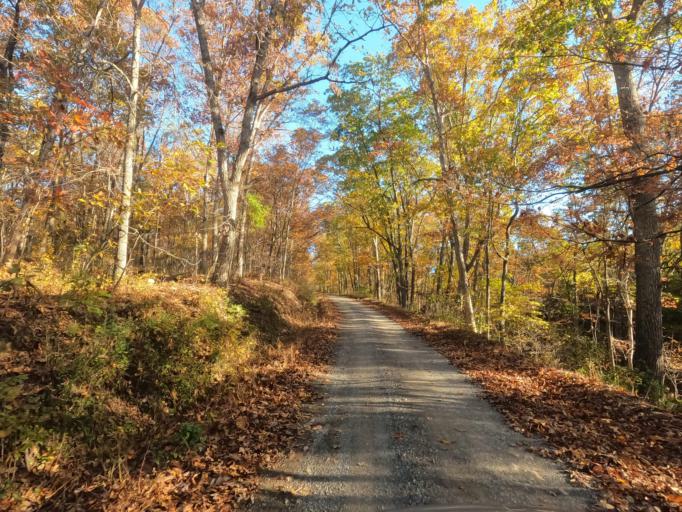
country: US
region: West Virginia
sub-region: Mineral County
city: Fort Ashby
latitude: 39.5299
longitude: -78.5378
